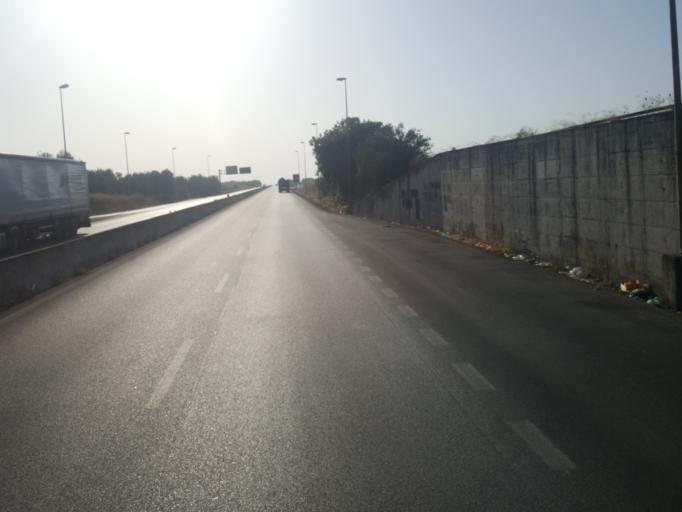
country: IT
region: Apulia
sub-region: Provincia di Barletta - Andria - Trani
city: San Ferdinando di Puglia
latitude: 41.3107
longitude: 16.0744
